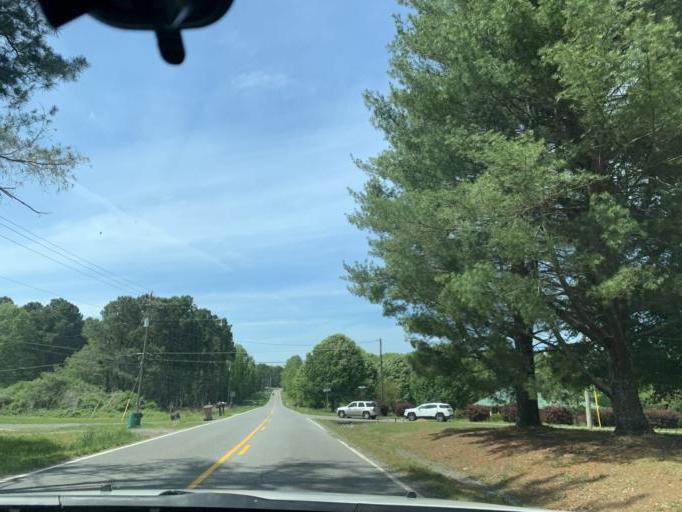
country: US
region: Georgia
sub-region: Forsyth County
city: Cumming
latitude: 34.2622
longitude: -84.1723
